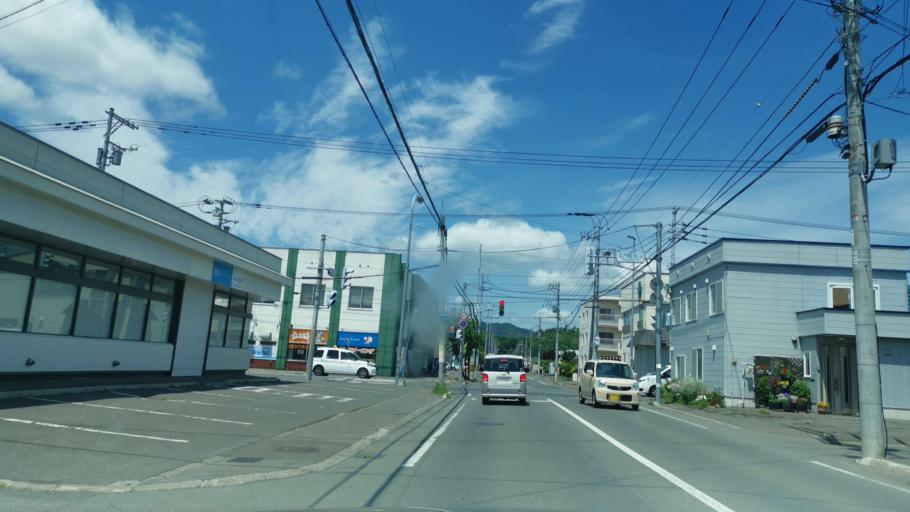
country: JP
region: Hokkaido
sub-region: Asahikawa-shi
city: Asahikawa
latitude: 43.7934
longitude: 142.3340
